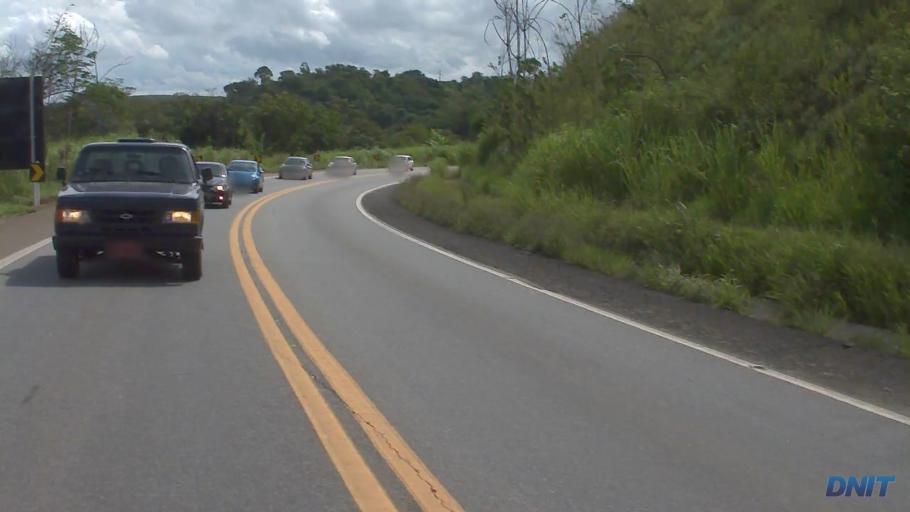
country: BR
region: Minas Gerais
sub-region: Ipaba
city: Ipaba
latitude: -19.3874
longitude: -42.4759
